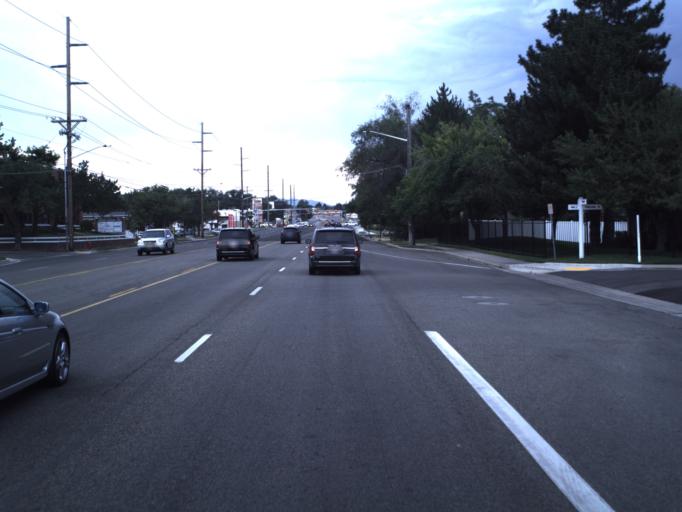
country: US
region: Utah
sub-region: Salt Lake County
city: Midvale
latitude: 40.6254
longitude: -111.8661
